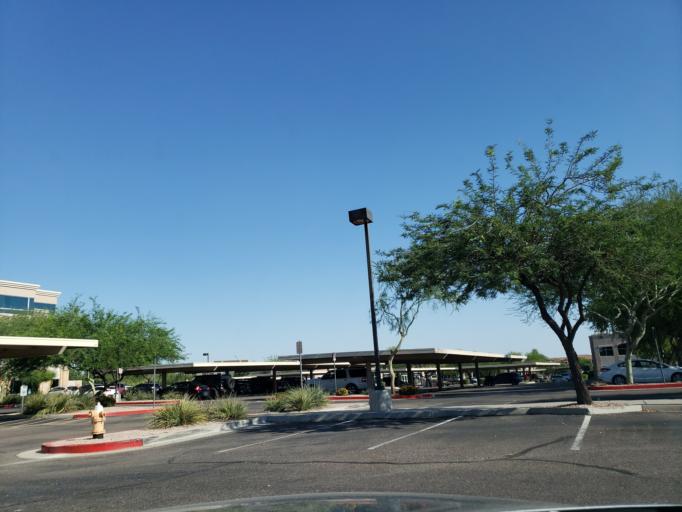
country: US
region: Arizona
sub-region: Maricopa County
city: Paradise Valley
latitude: 33.6545
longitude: -111.9311
